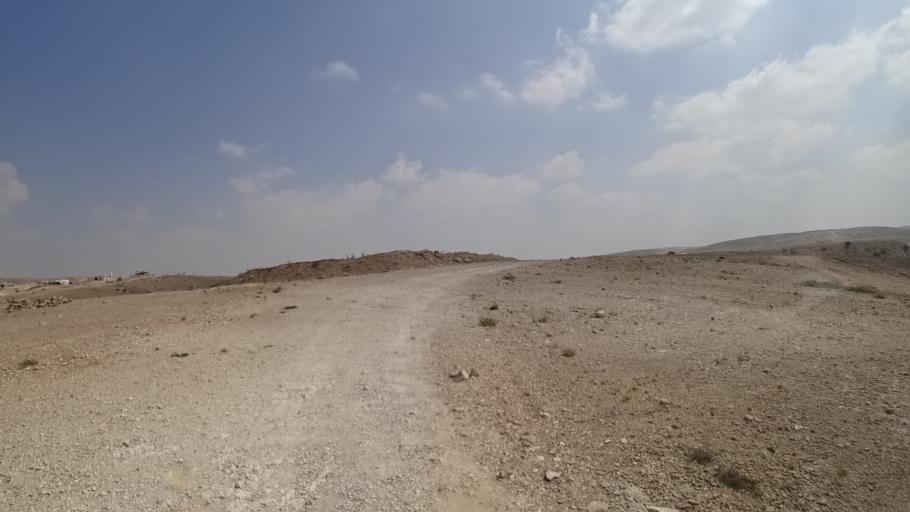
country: OM
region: Zufar
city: Salalah
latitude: 17.2447
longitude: 53.8902
